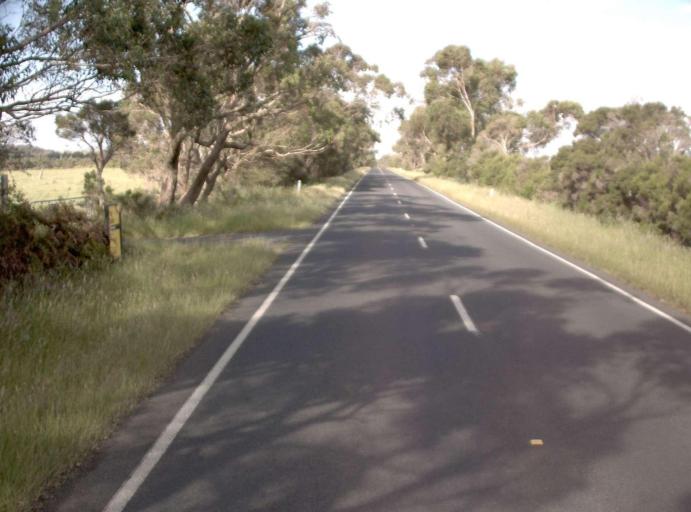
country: AU
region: Victoria
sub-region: Bass Coast
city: North Wonthaggi
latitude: -38.5940
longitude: 145.7919
